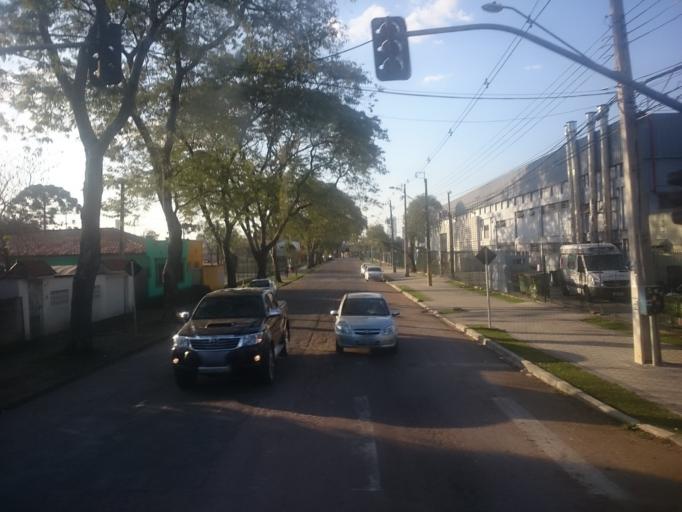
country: BR
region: Parana
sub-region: Curitiba
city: Curitiba
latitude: -25.4502
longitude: -49.2541
